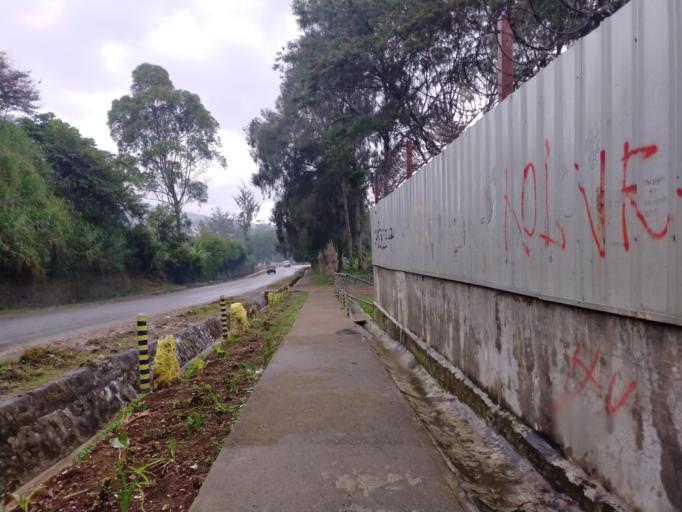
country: PG
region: Southern Highlands
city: Mendi
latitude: -6.1318
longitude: 143.6537
